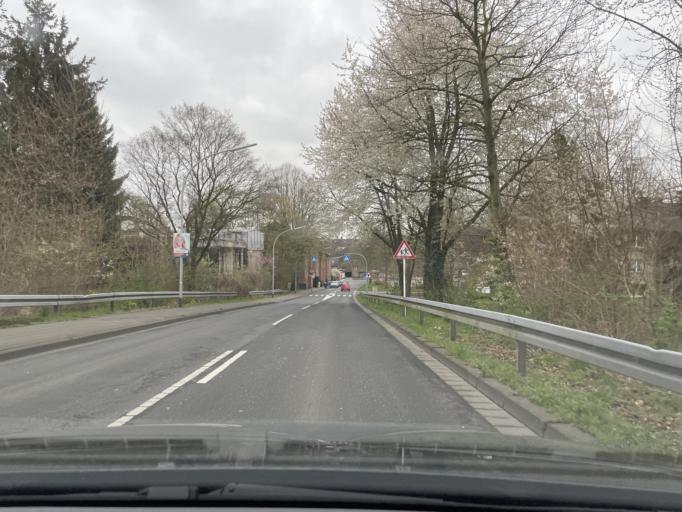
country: DE
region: North Rhine-Westphalia
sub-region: Regierungsbezirk Dusseldorf
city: Monchengladbach
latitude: 51.1247
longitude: 6.4369
